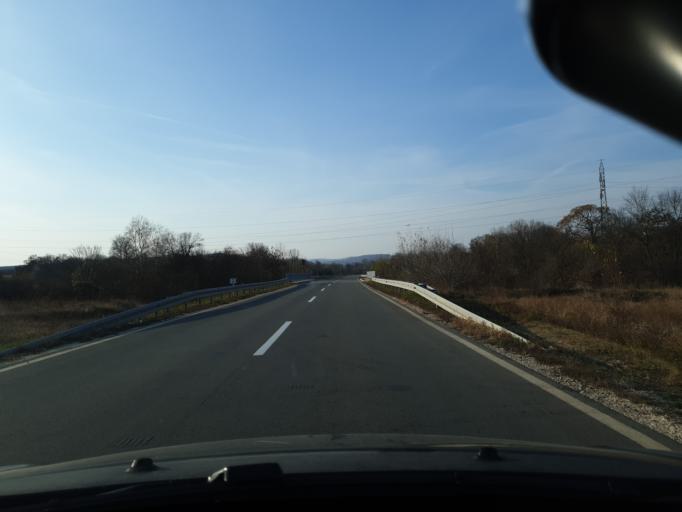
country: RS
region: Central Serbia
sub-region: Zajecarski Okrug
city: Zajecar
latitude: 43.9494
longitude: 22.2898
